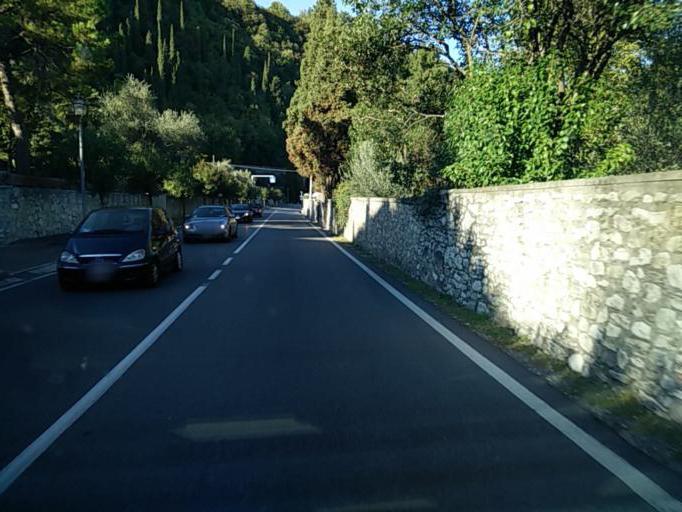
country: IT
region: Lombardy
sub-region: Provincia di Brescia
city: Gardone Riviera
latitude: 45.6280
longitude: 10.5867
